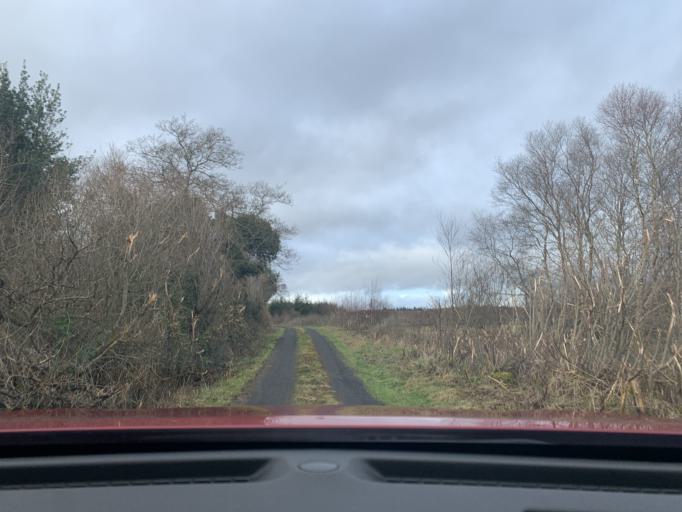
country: IE
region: Connaught
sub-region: Roscommon
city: Ballaghaderreen
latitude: 53.9268
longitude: -8.5593
